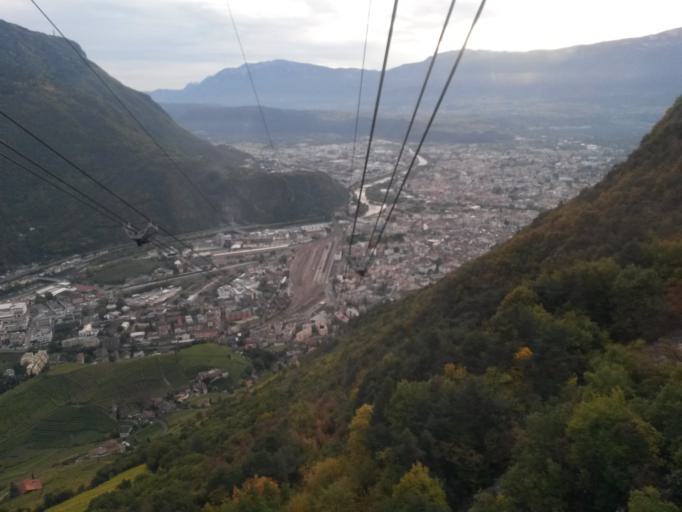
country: IT
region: Trentino-Alto Adige
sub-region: Bolzano
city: Cardano
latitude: 46.5080
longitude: 11.3758
